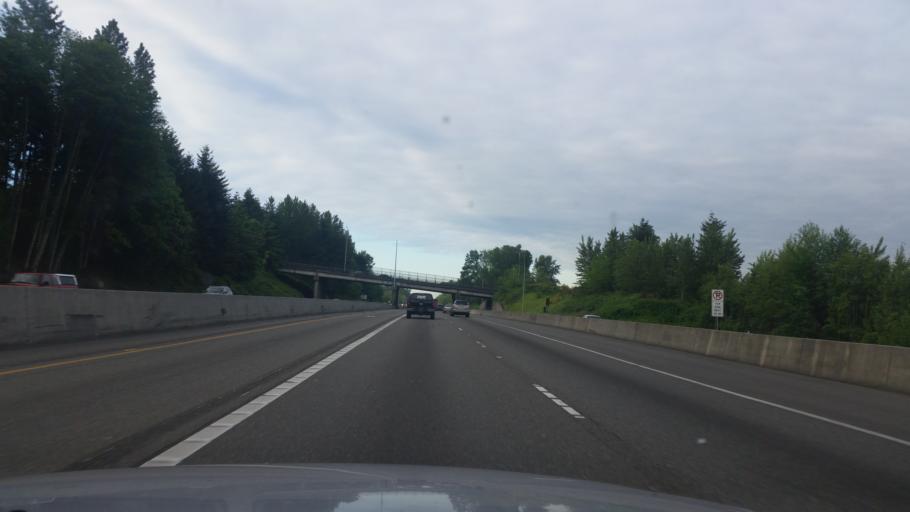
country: US
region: Washington
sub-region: King County
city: Renton
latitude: 47.4432
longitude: -122.2171
